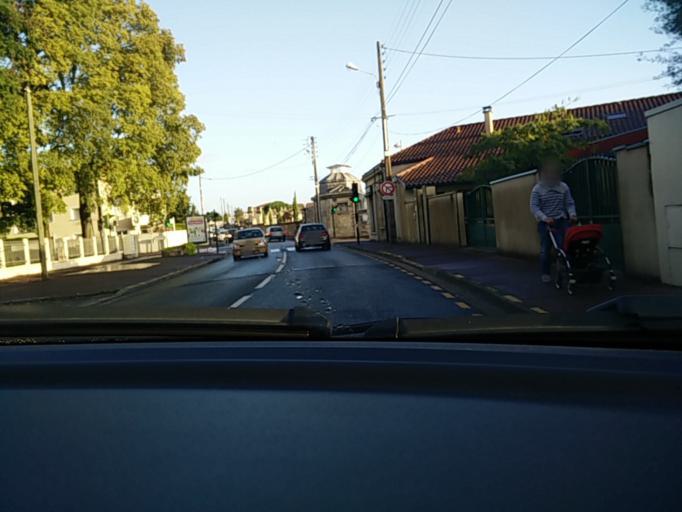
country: FR
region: Aquitaine
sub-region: Departement de la Gironde
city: Le Bouscat
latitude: 44.8656
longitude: -0.5950
